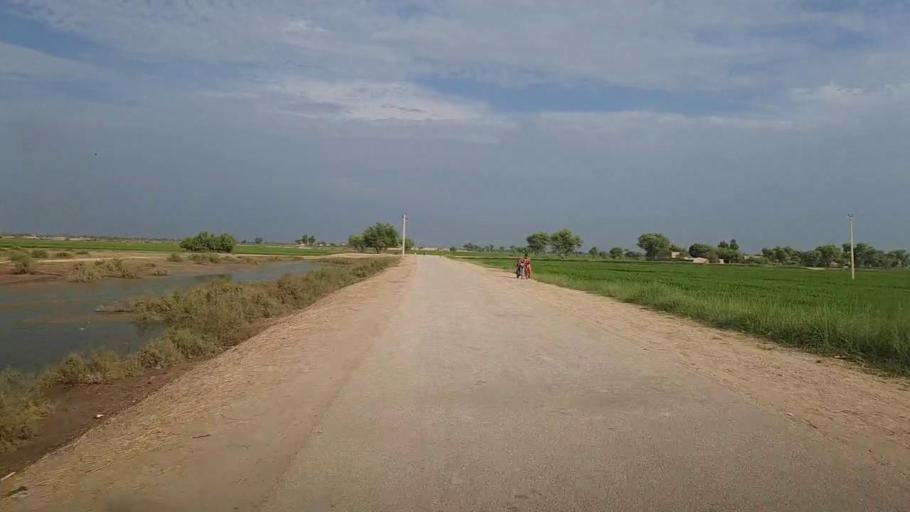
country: PK
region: Sindh
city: Thul
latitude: 28.2645
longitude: 68.8580
